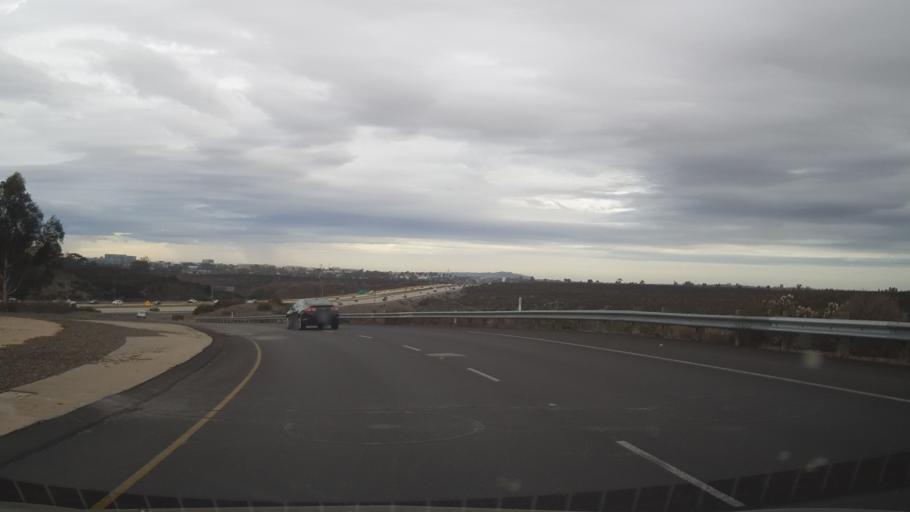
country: US
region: California
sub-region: San Diego County
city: La Mesa
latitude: 32.8430
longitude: -117.0977
